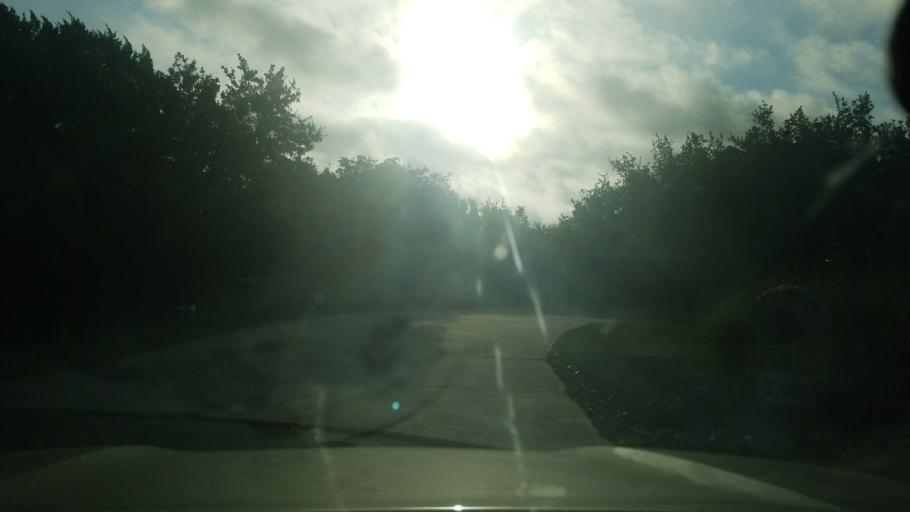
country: US
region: Texas
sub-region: Bexar County
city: Timberwood Park
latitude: 29.7005
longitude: -98.4979
